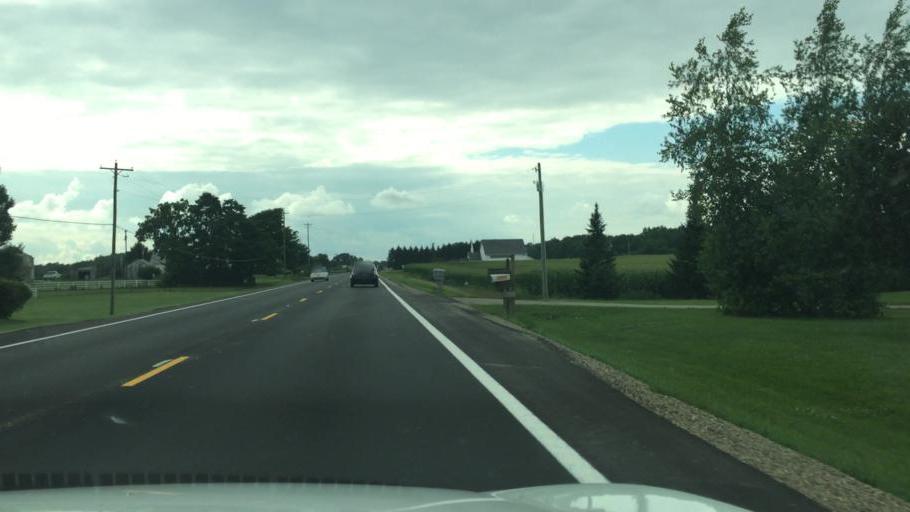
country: US
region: Ohio
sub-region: Champaign County
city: Urbana
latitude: 40.0922
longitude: -83.6972
